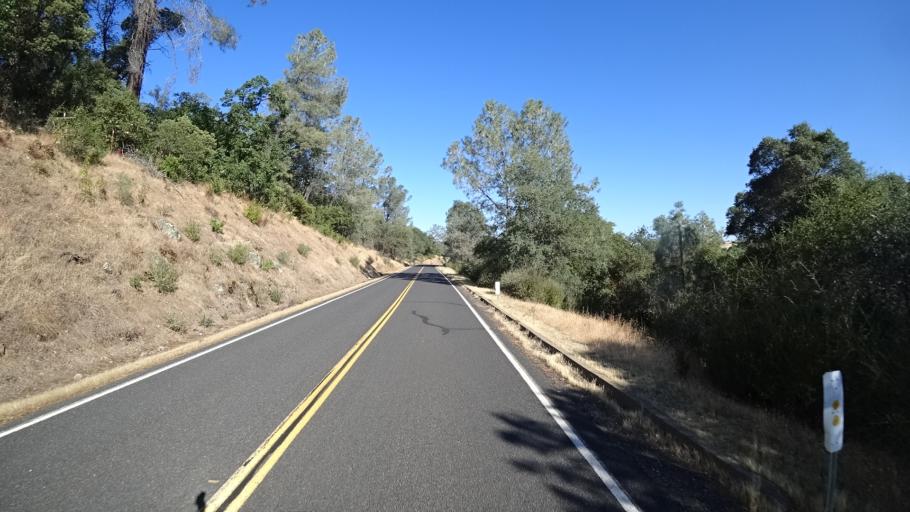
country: US
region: California
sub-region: Calaveras County
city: Murphys
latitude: 38.0832
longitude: -120.4827
